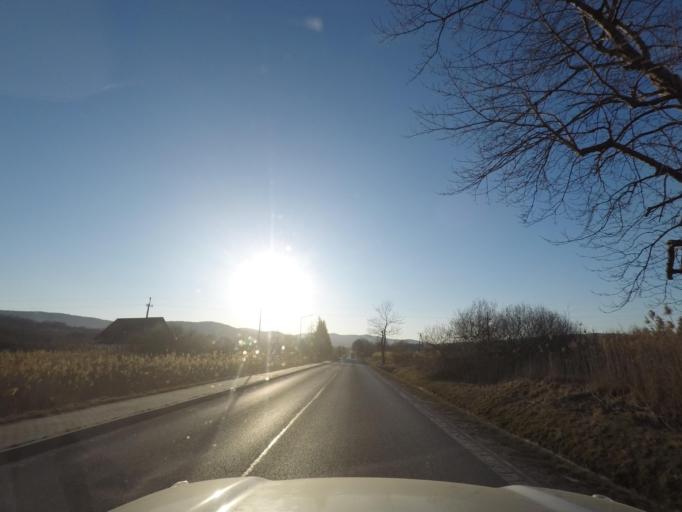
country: PL
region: Subcarpathian Voivodeship
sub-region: Powiat krosnienski
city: Dukla
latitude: 49.5577
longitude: 21.6427
